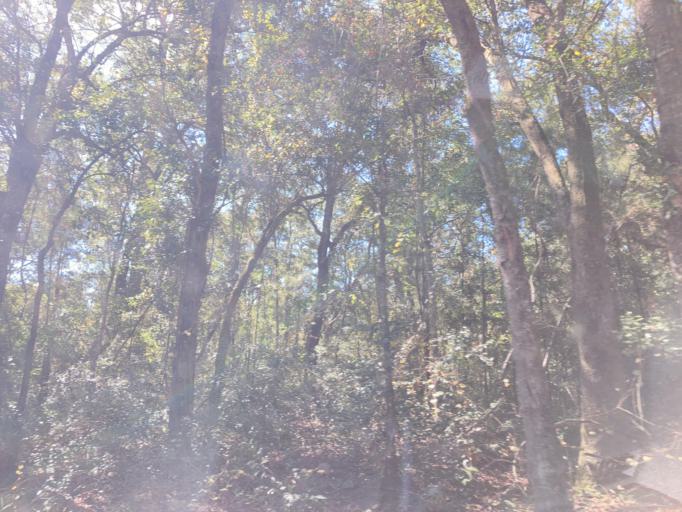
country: US
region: Mississippi
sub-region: Jackson County
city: Gulf Hills
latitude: 30.4516
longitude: -88.8347
